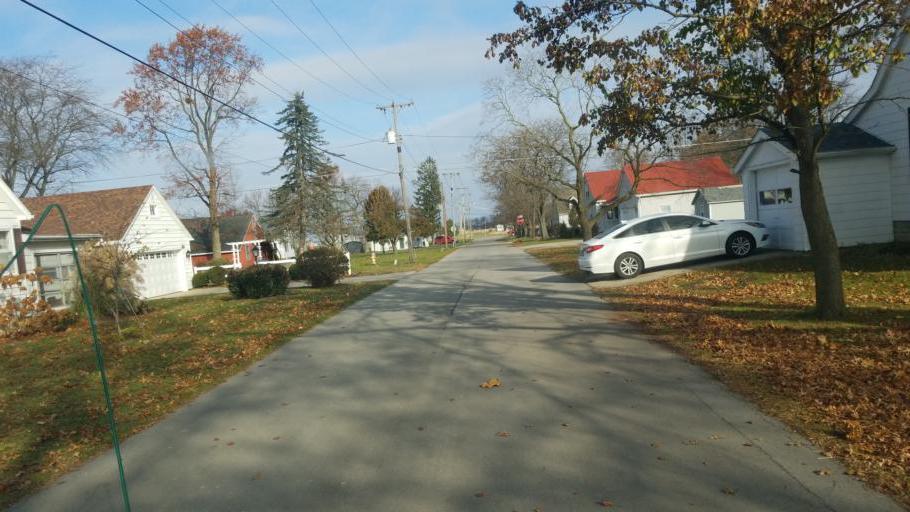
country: US
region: Indiana
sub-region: Adams County
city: Berne
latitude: 40.6586
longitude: -84.9597
